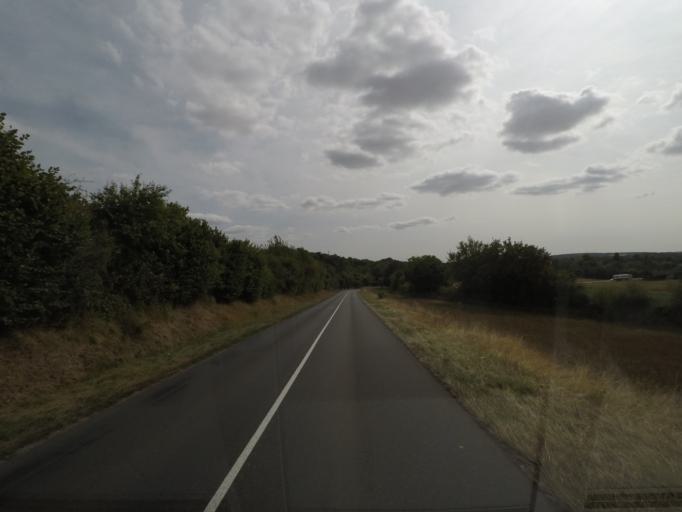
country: FR
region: Poitou-Charentes
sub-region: Departement de la Charente
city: Ruffec
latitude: 46.0259
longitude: 0.2337
